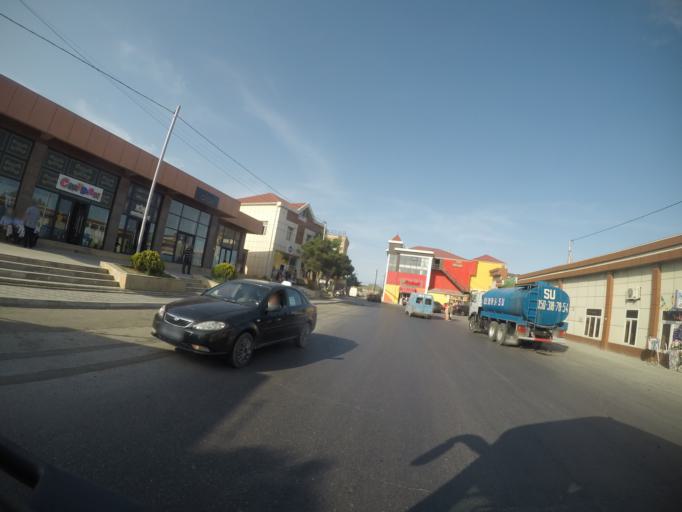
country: AZ
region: Baki
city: Binagadi
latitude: 40.4673
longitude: 49.8417
